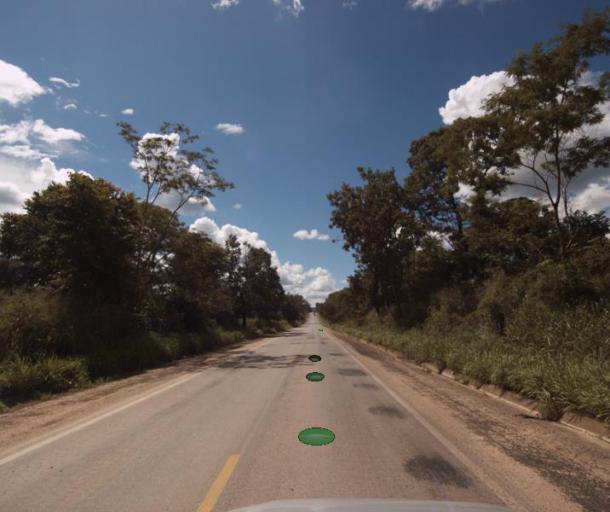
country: BR
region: Goias
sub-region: Porangatu
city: Porangatu
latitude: -13.6989
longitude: -49.0217
